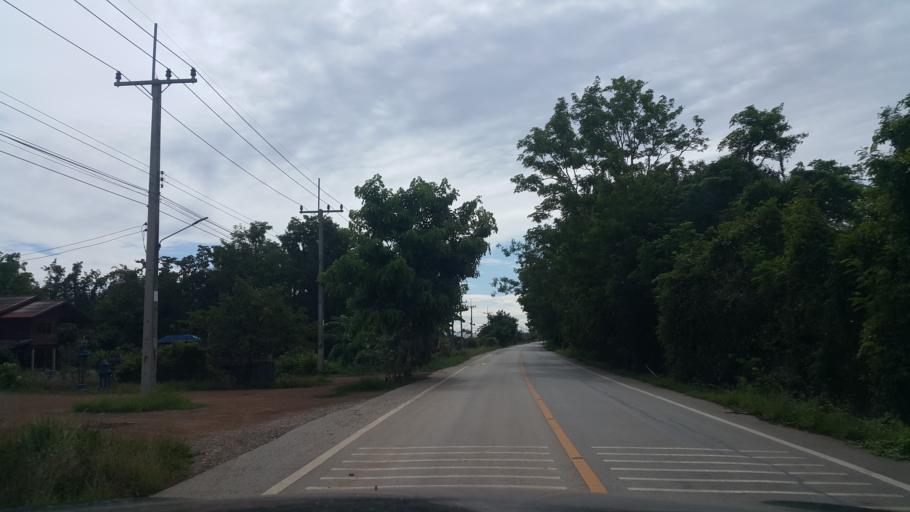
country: TH
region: Sukhothai
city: Si Nakhon
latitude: 17.2819
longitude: 100.0098
